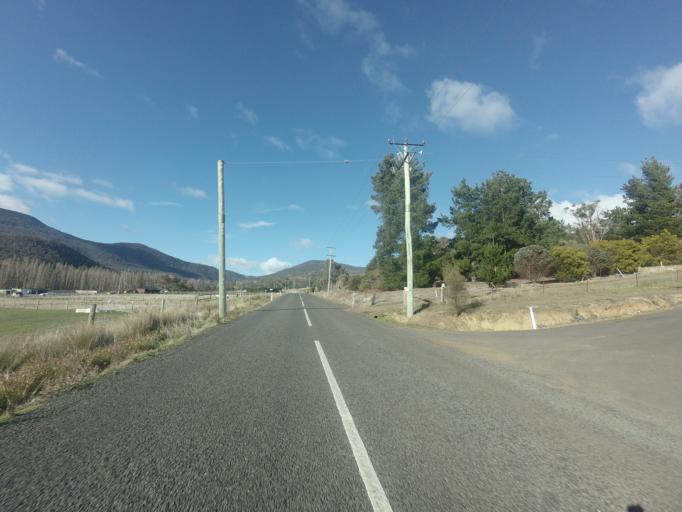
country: AU
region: Tasmania
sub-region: Derwent Valley
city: New Norfolk
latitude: -42.7979
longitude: 147.1330
